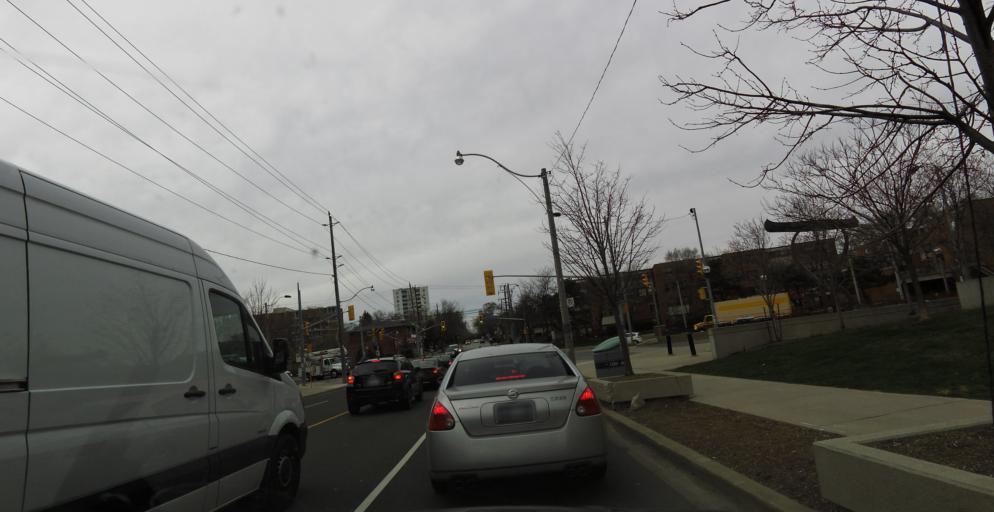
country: CA
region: Ontario
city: Toronto
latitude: 43.6368
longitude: -79.4695
